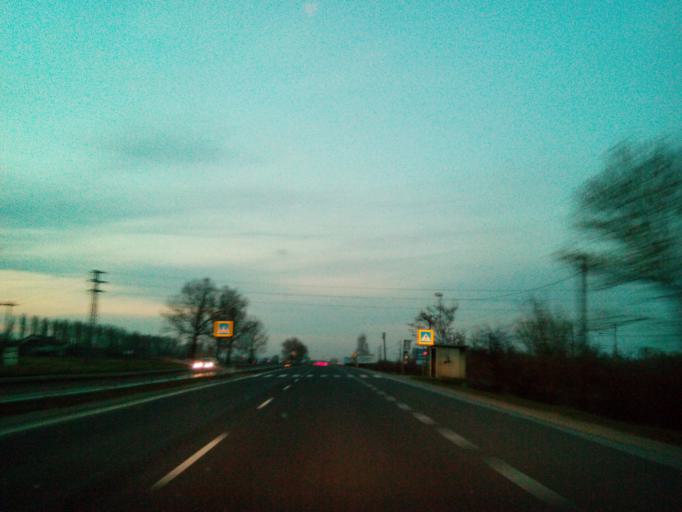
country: SK
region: Kosicky
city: Kosice
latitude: 48.6419
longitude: 21.2010
